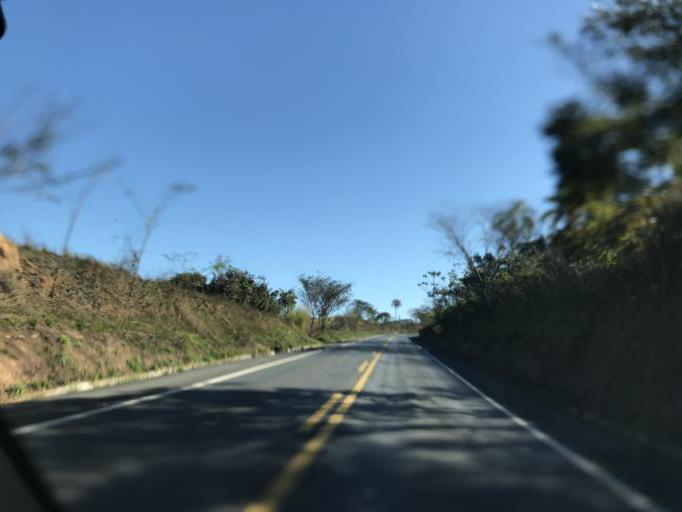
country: BR
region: Minas Gerais
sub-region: Campos Altos
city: Campos Altos
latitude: -19.8180
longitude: -46.0247
